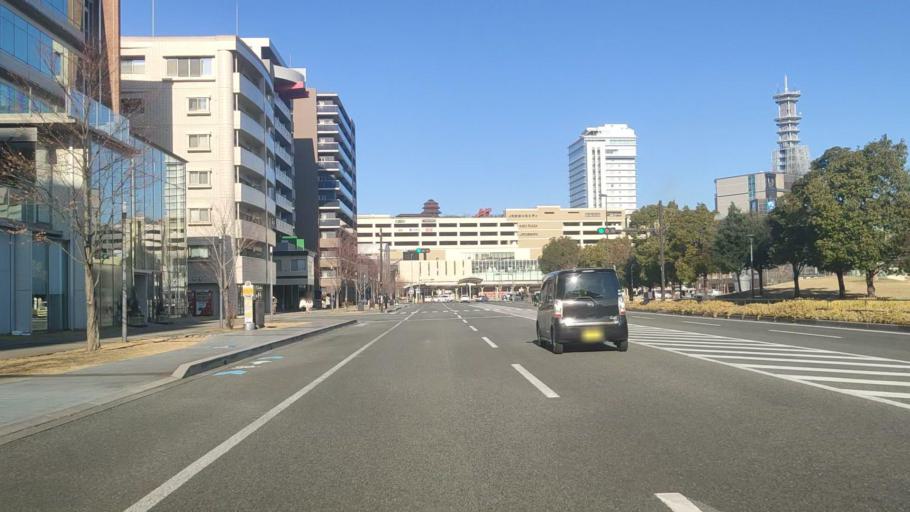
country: JP
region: Oita
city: Oita
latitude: 33.2304
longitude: 131.6038
